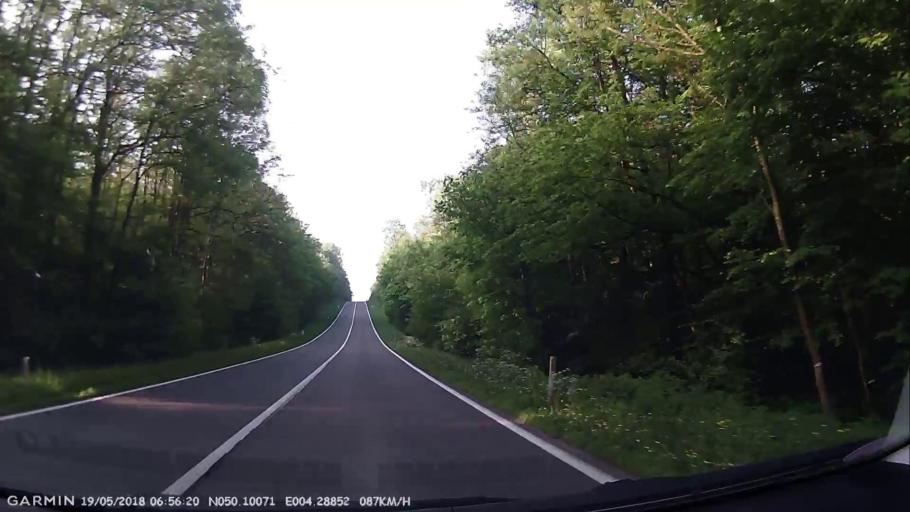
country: BE
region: Wallonia
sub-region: Province du Hainaut
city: Chimay
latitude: 50.1006
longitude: 4.2885
